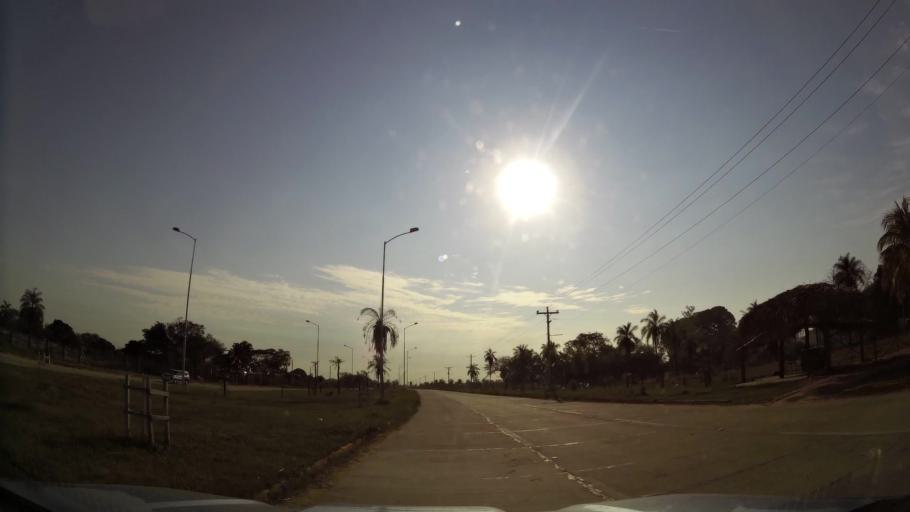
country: BO
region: Santa Cruz
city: Santa Cruz de la Sierra
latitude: -17.6986
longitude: -63.1251
